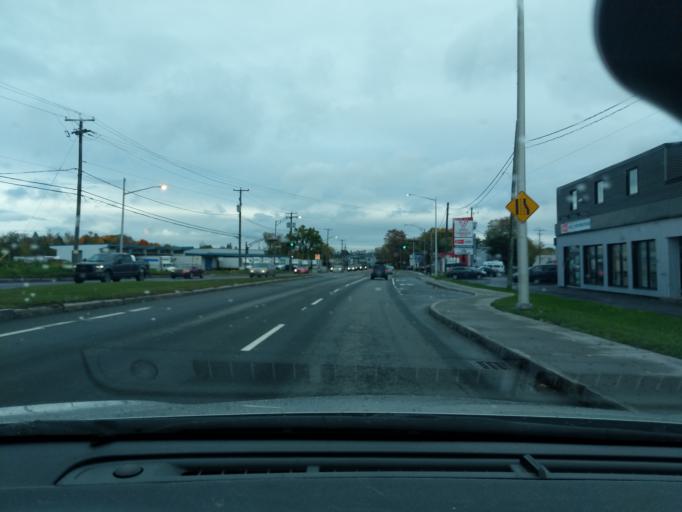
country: CA
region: Quebec
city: L'Ancienne-Lorette
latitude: 46.8062
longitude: -71.2885
